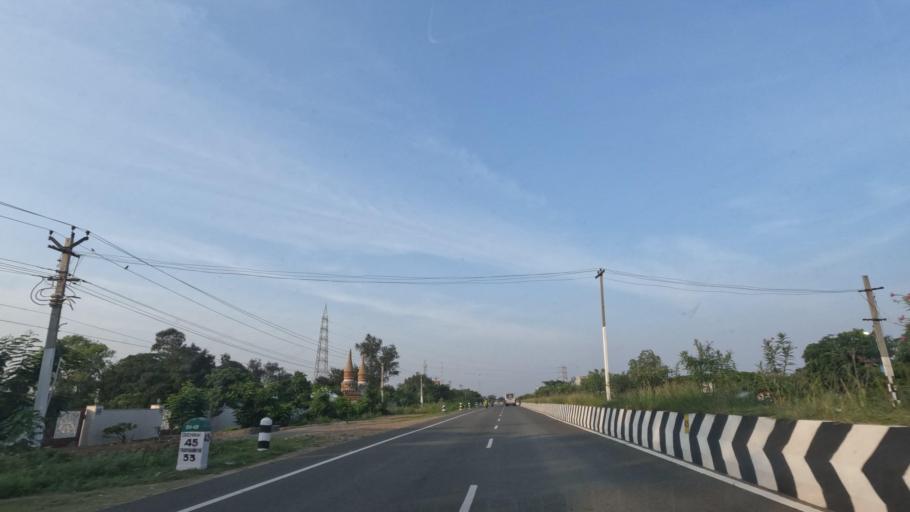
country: IN
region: Tamil Nadu
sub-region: Kancheepuram
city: Mamallapuram
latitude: 12.7006
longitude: 80.2219
